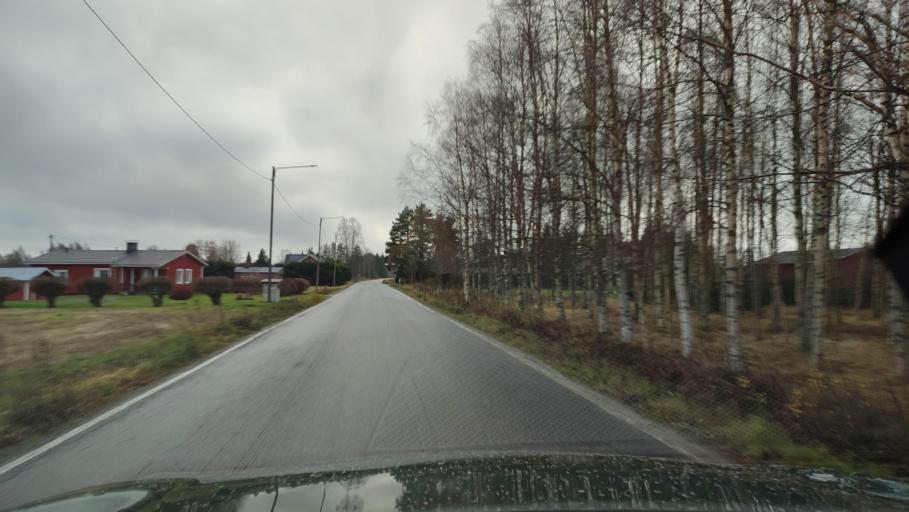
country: FI
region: Southern Ostrobothnia
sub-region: Suupohja
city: Teuva
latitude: 62.4500
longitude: 21.5987
